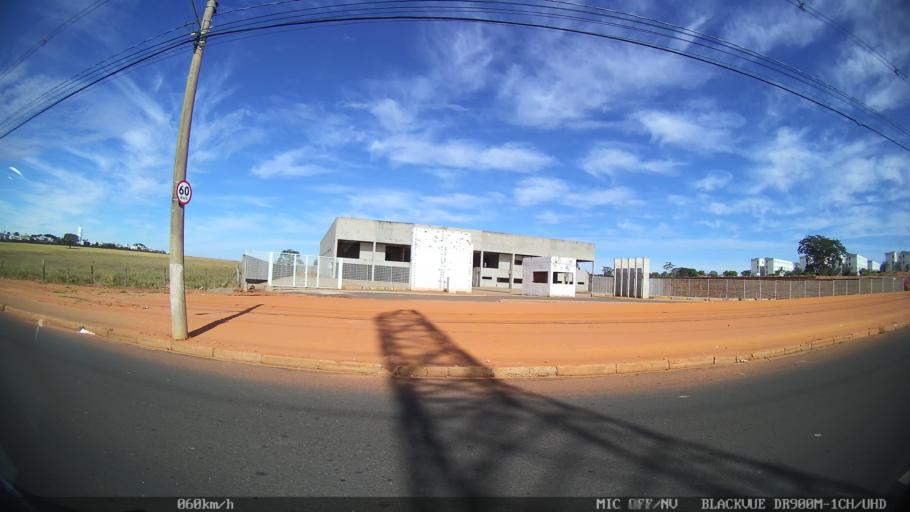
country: BR
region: Sao Paulo
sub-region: Sao Jose Do Rio Preto
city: Sao Jose do Rio Preto
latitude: -20.8166
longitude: -49.4883
